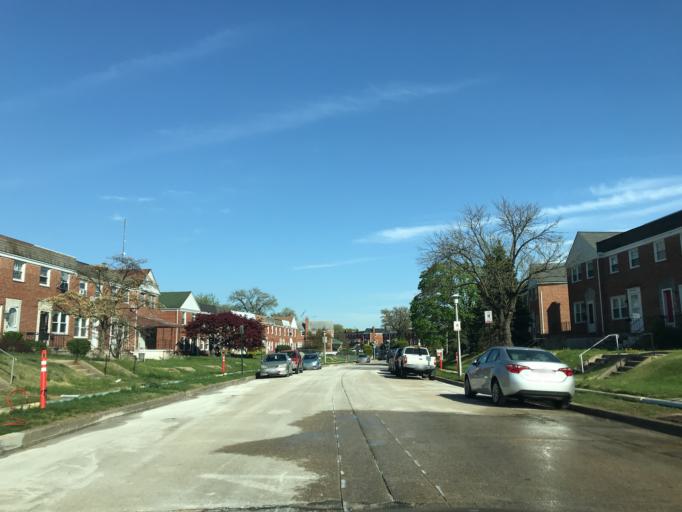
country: US
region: Maryland
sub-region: Baltimore County
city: Rosedale
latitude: 39.3238
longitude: -76.5586
